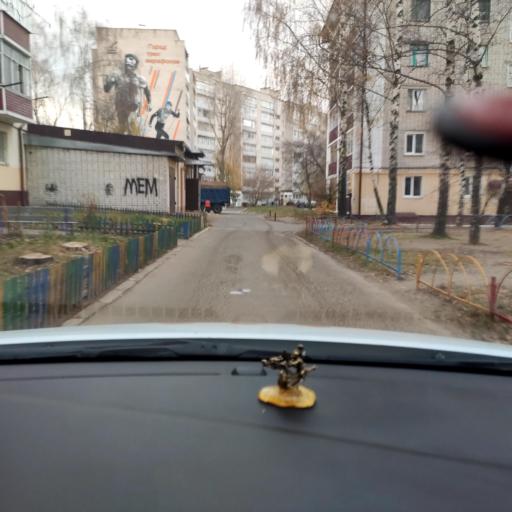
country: RU
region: Tatarstan
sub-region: Zelenodol'skiy Rayon
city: Zelenodolsk
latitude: 55.8489
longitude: 48.5590
